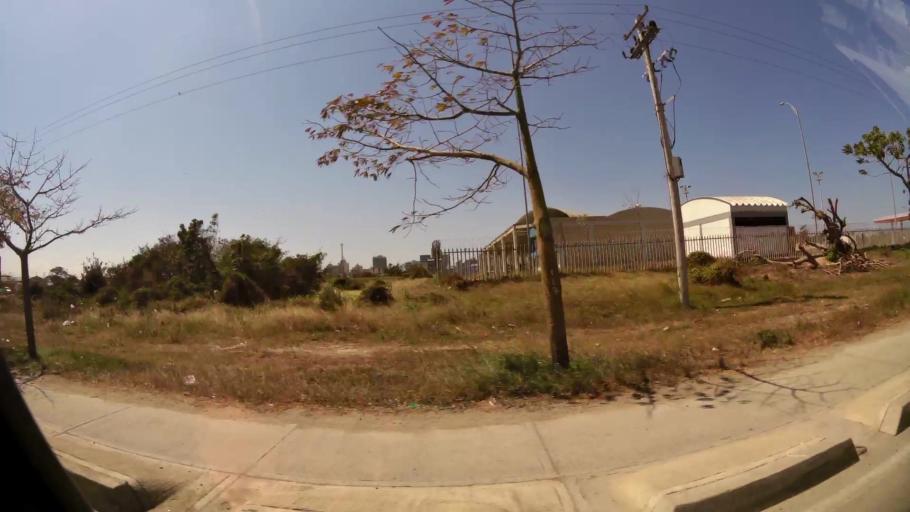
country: CO
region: Atlantico
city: Barranquilla
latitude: 10.9845
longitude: -74.7704
